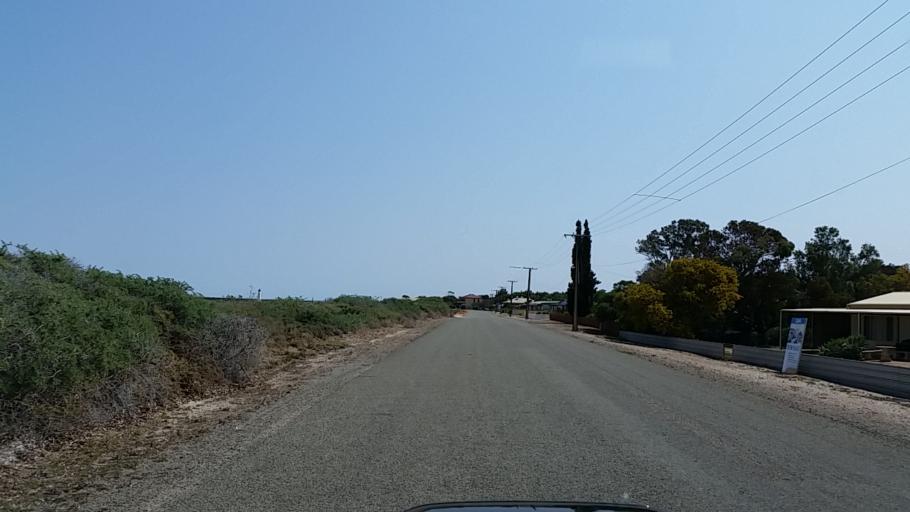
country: AU
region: South Australia
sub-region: Port Pirie City and Dists
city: Port Pirie
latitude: -33.0248
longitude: 138.0034
